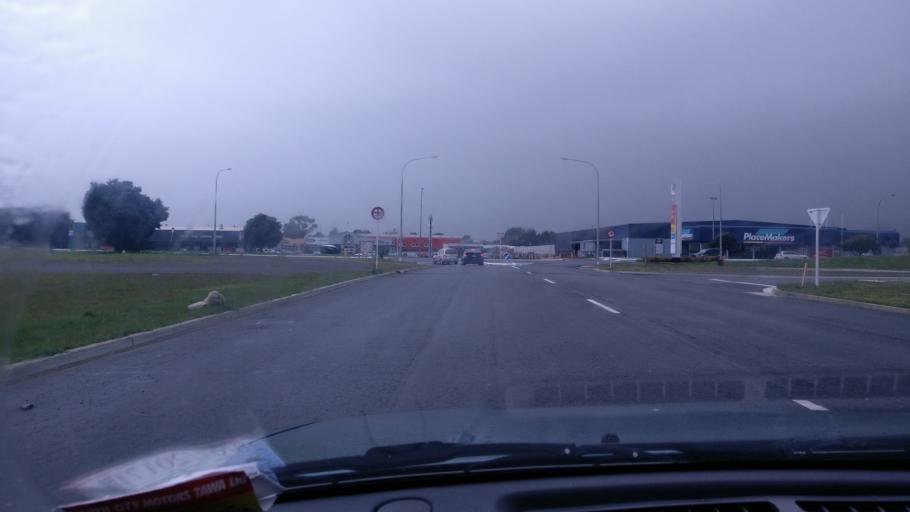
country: NZ
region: Wellington
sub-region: Kapiti Coast District
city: Paraparaumu
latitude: -40.9043
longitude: 174.9940
